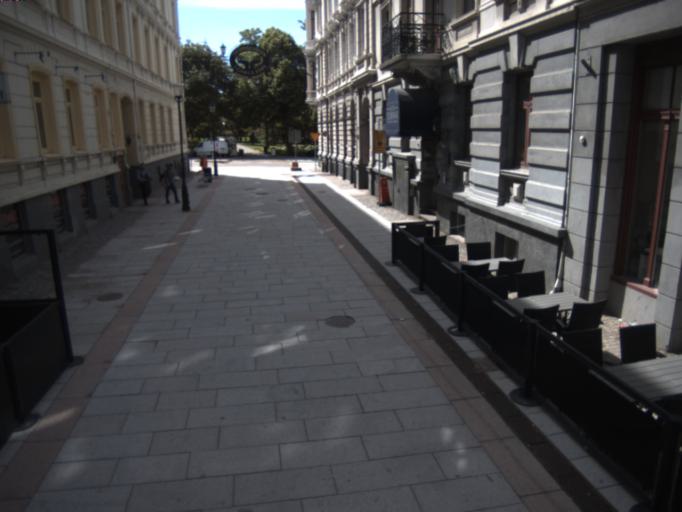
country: SE
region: Skane
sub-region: Helsingborg
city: Helsingborg
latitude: 56.0437
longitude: 12.6974
